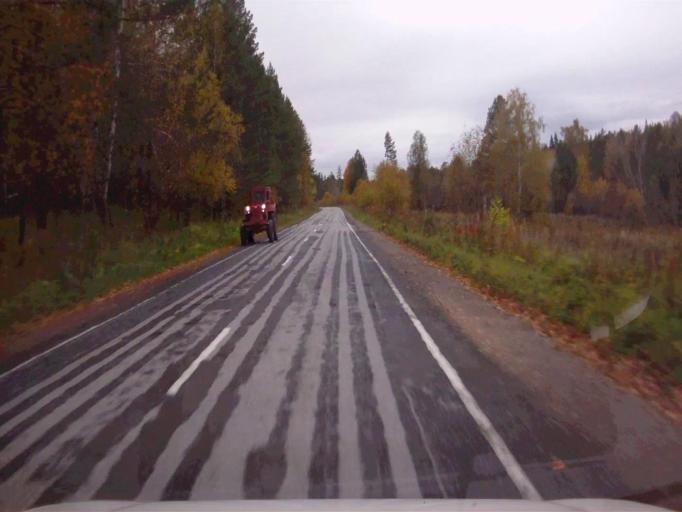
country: RU
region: Chelyabinsk
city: Nyazepetrovsk
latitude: 56.0513
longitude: 59.4859
